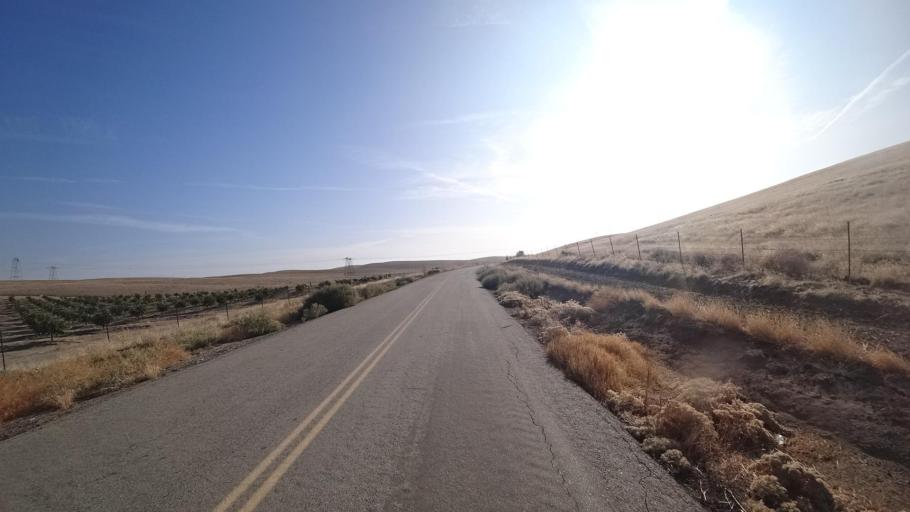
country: US
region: California
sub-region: Tulare County
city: Richgrove
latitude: 35.6418
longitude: -119.0468
